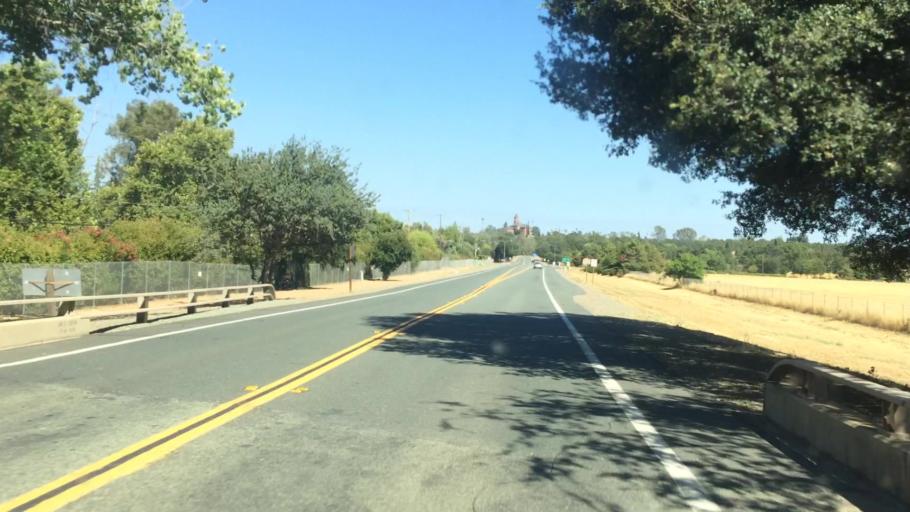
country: US
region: California
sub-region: Amador County
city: Ione
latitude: 38.3663
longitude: -120.9529
